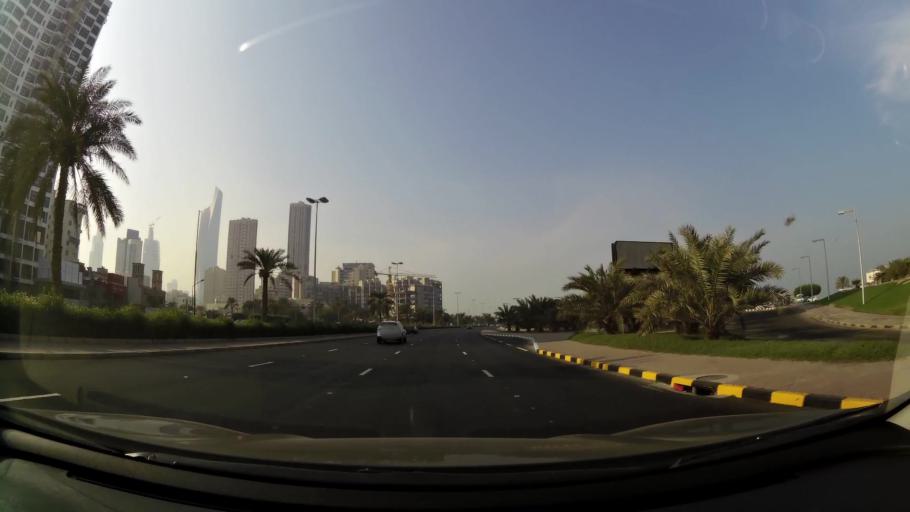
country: KW
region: Al Asimah
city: Ad Dasmah
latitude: 29.3743
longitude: 48.0060
